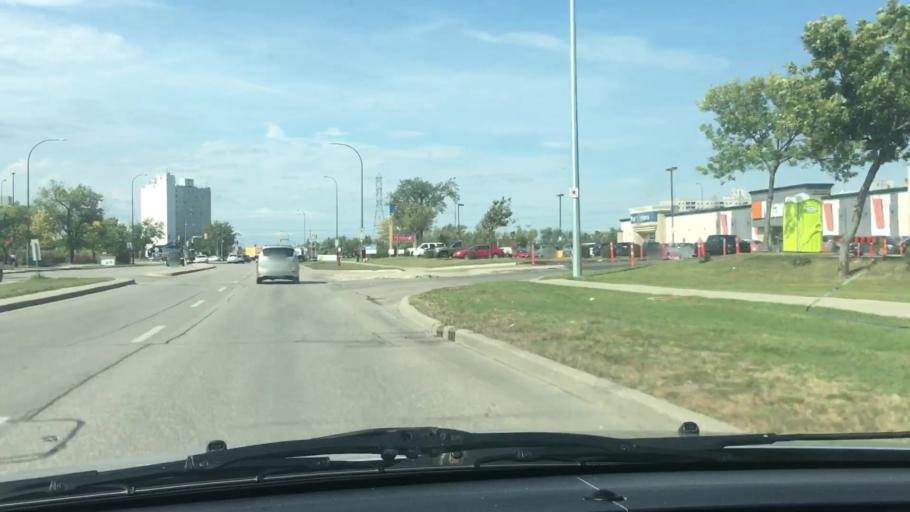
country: CA
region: Manitoba
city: Winnipeg
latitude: 49.8308
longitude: -97.1071
